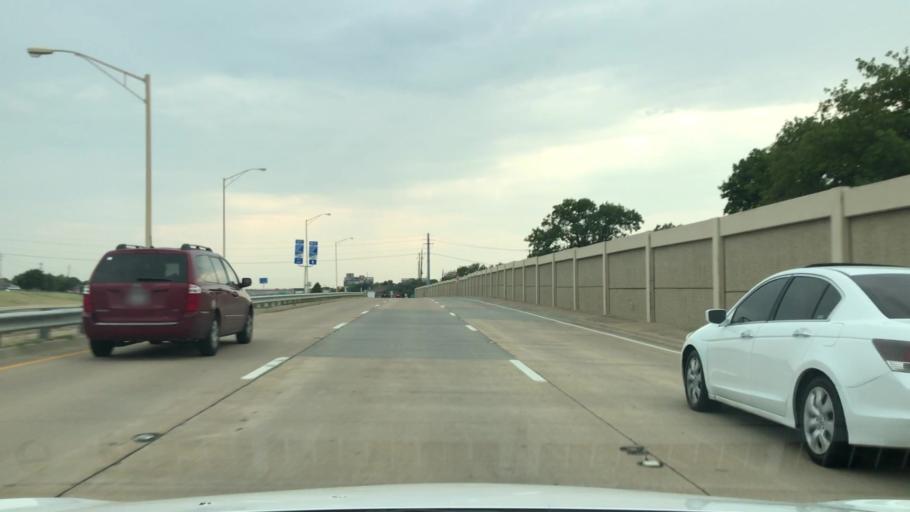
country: US
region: Texas
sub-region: Dallas County
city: Carrollton
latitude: 32.9862
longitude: -96.8859
